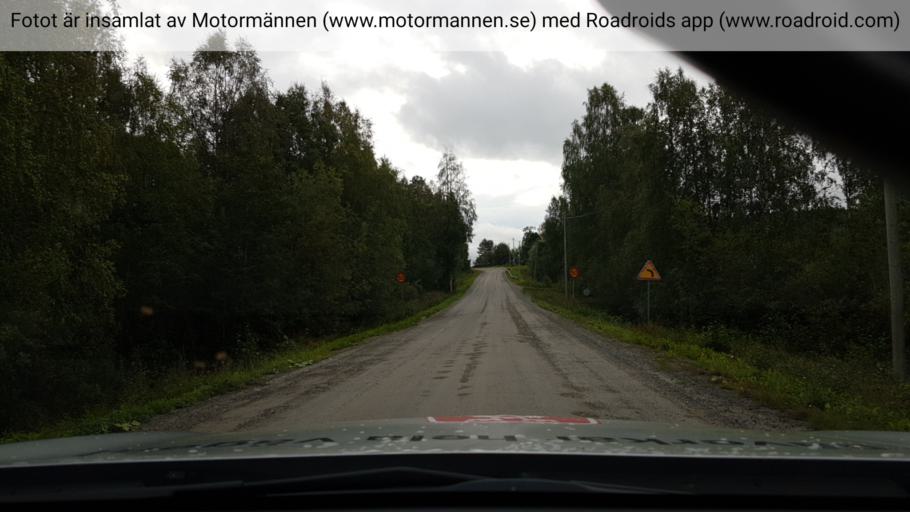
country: SE
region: Vaesterbotten
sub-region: Vannas Kommun
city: Vannasby
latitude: 64.1003
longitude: 20.0019
